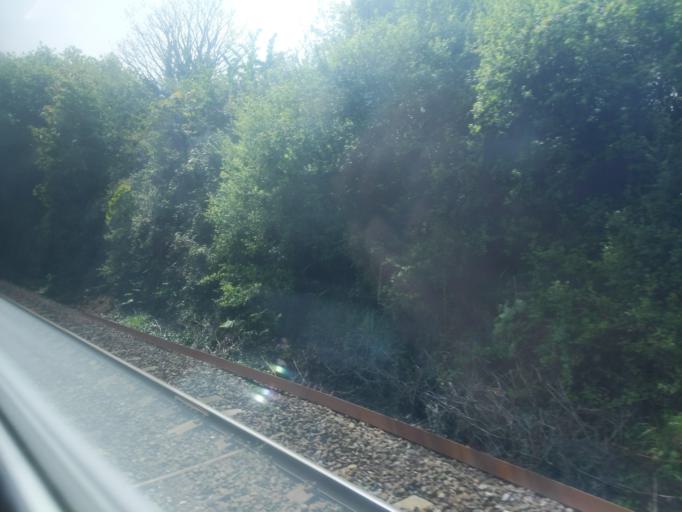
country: GB
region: England
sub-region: Cornwall
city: Hayle
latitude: 50.1648
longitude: -5.4511
